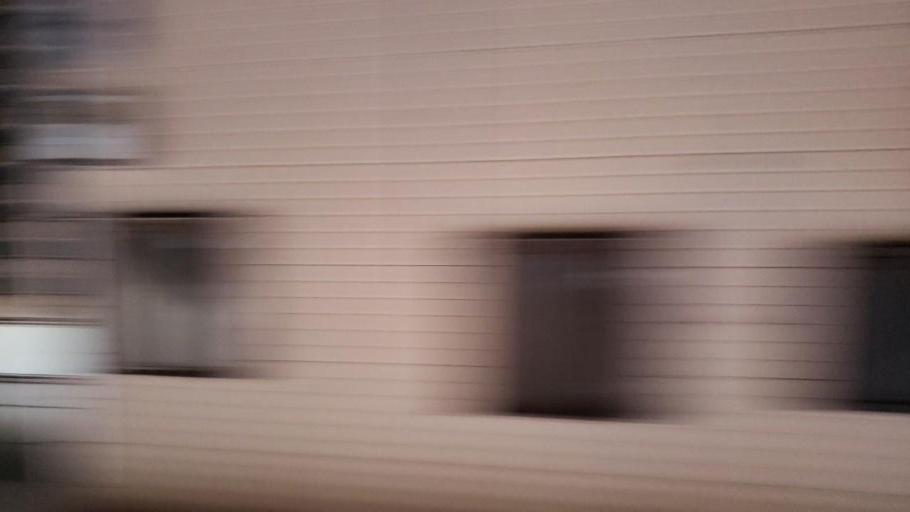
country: JP
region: Tokushima
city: Kamojimacho-jogejima
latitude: 34.1021
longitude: 134.3188
